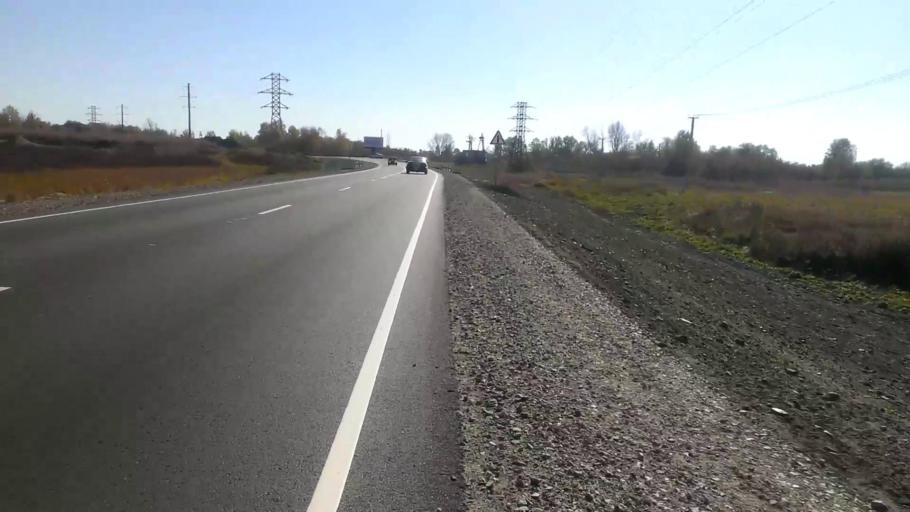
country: RU
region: Altai Krai
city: Sannikovo
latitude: 53.3311
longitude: 83.9383
